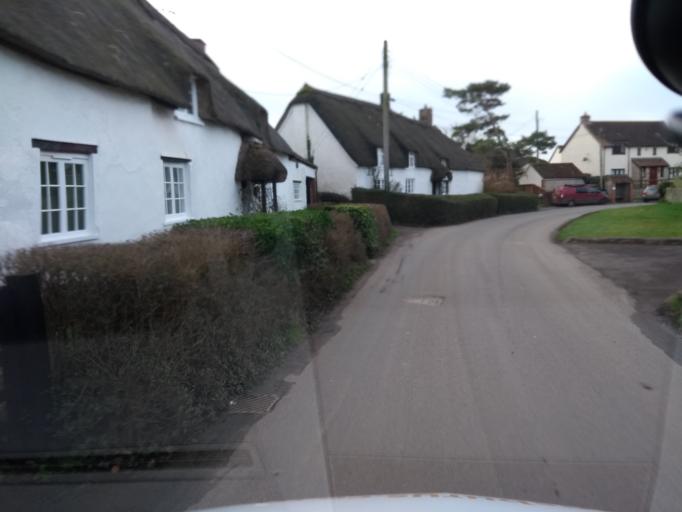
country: GB
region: England
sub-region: Somerset
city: Westonzoyland
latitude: 51.0905
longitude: -2.8918
